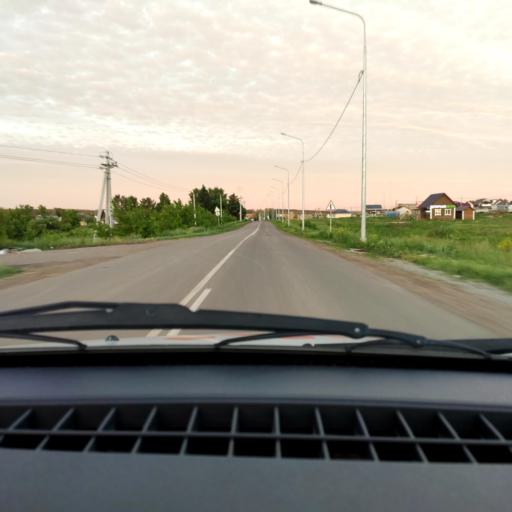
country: RU
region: Bashkortostan
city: Avdon
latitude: 54.5572
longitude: 55.7624
